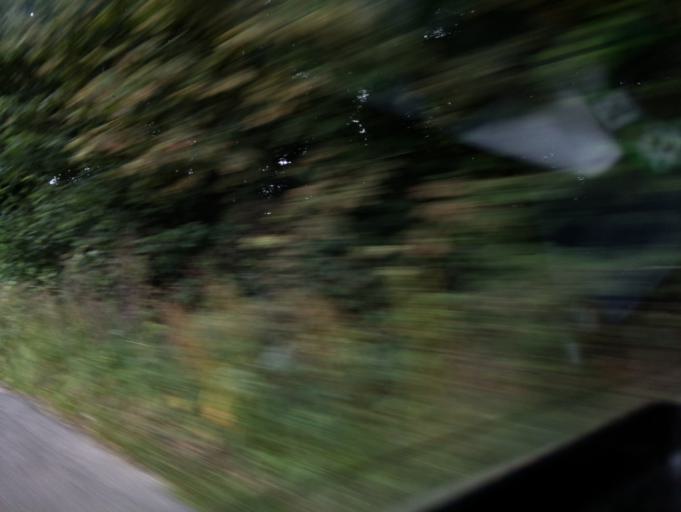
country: GB
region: England
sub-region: Gloucestershire
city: Chalford
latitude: 51.7841
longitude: -2.1093
